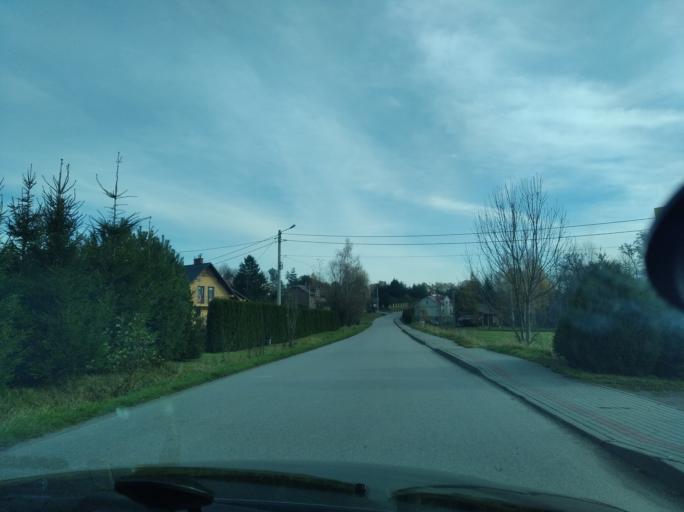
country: PL
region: Subcarpathian Voivodeship
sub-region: Powiat lancucki
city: Kraczkowa
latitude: 50.0388
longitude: 22.1931
